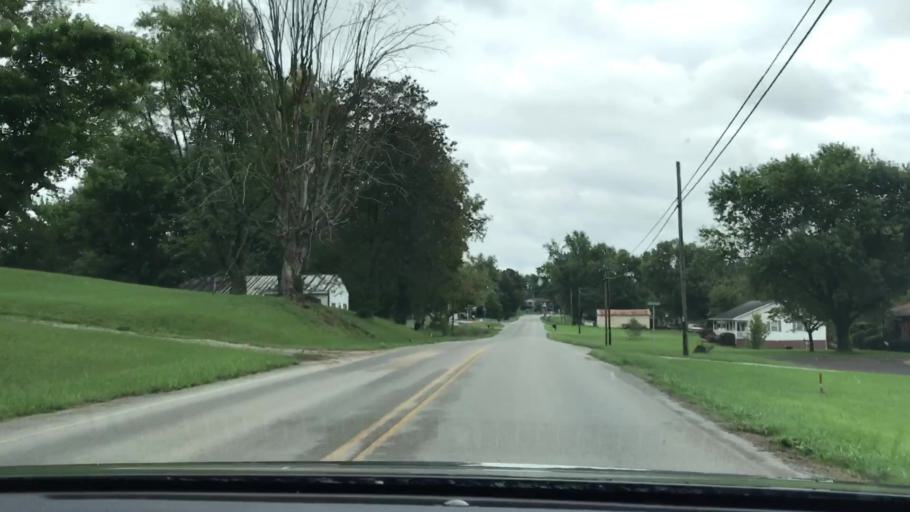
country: US
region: Kentucky
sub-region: Barren County
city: Glasgow
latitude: 36.9638
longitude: -85.8703
